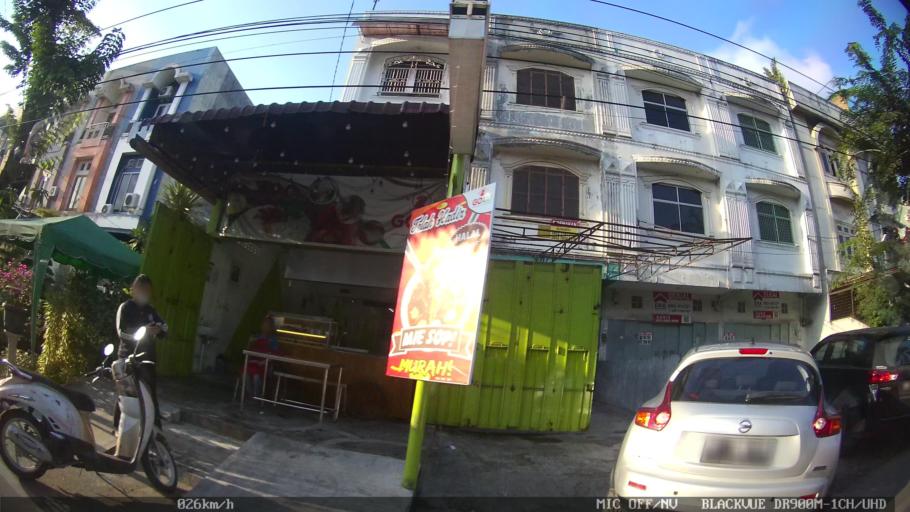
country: ID
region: North Sumatra
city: Medan
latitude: 3.6072
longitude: 98.6658
